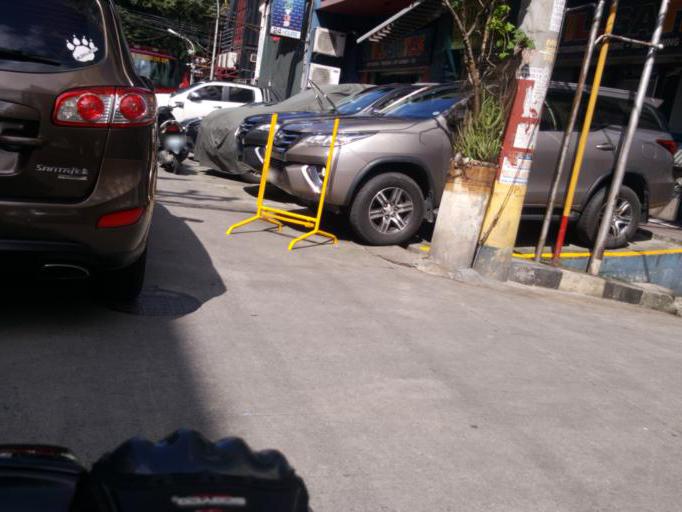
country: PH
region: Metro Manila
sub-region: City of Manila
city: Manila
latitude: 14.6084
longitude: 120.9869
